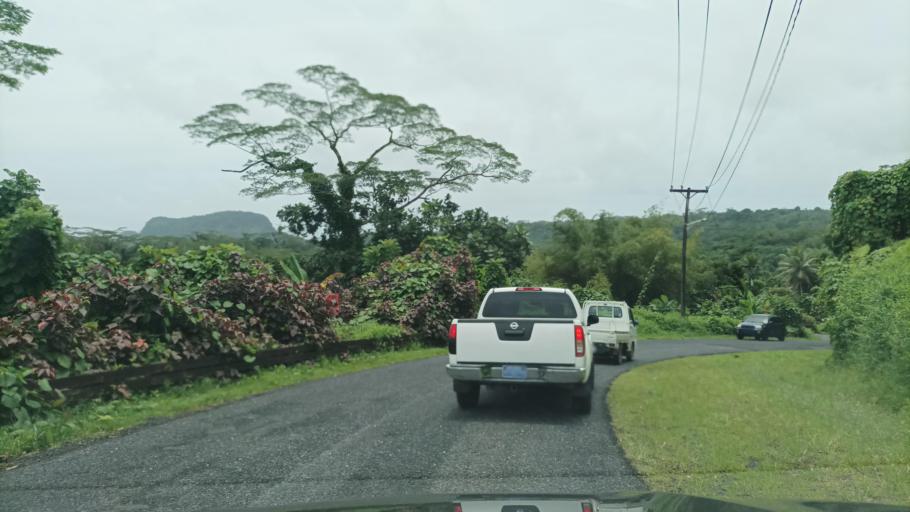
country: FM
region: Pohnpei
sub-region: Sokehs Municipality
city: Palikir - National Government Center
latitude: 6.9283
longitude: 158.1757
